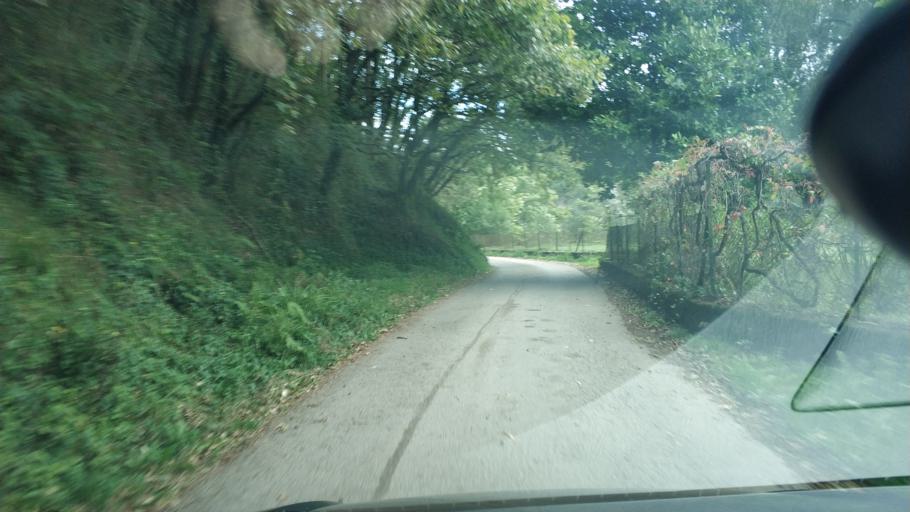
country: ES
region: Cantabria
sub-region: Provincia de Cantabria
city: Santa Maria de Cayon
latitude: 43.2968
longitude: -3.8554
